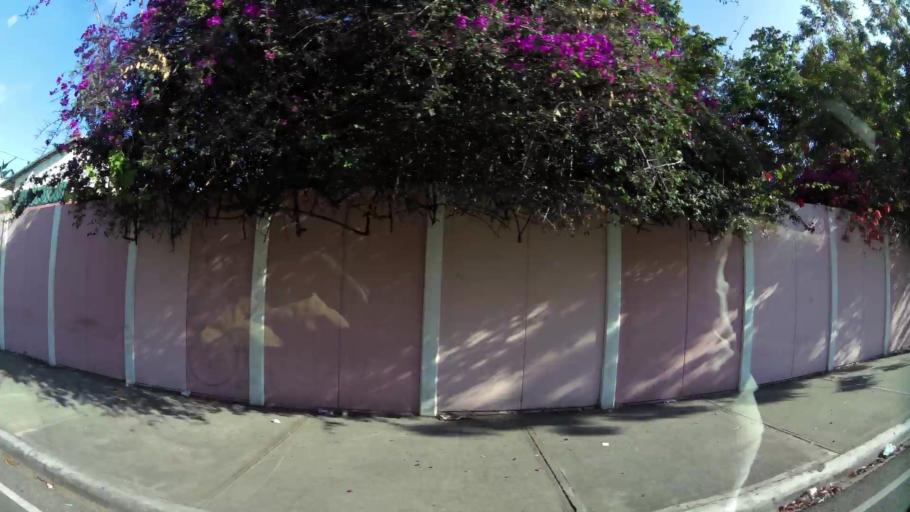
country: DO
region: Nacional
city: La Julia
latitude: 18.4579
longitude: -69.9190
